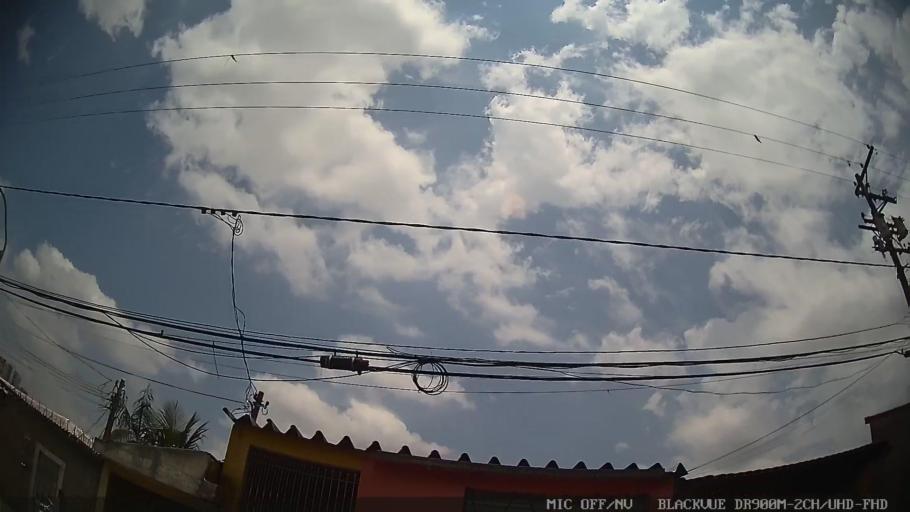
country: BR
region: Sao Paulo
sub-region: Osasco
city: Osasco
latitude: -23.4796
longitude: -46.7200
